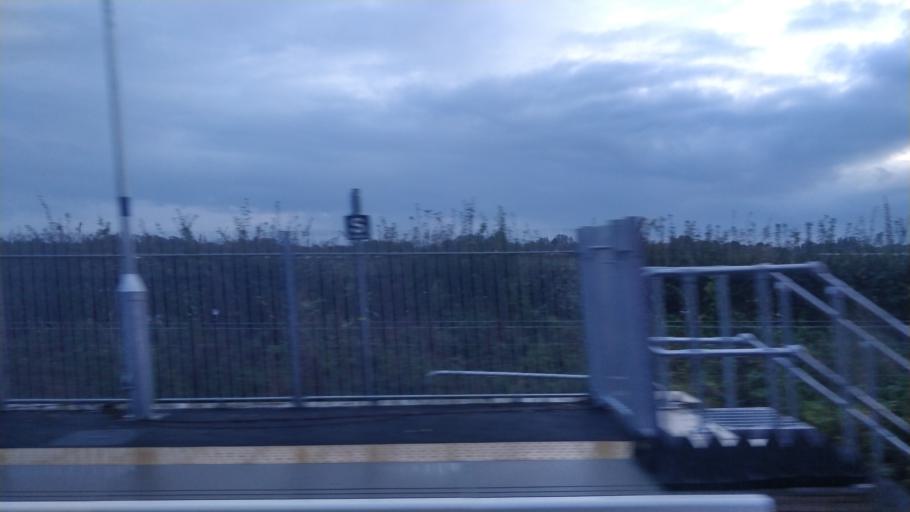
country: GB
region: England
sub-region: Lancashire
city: Ormskirk
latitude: 53.6121
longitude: -2.8691
